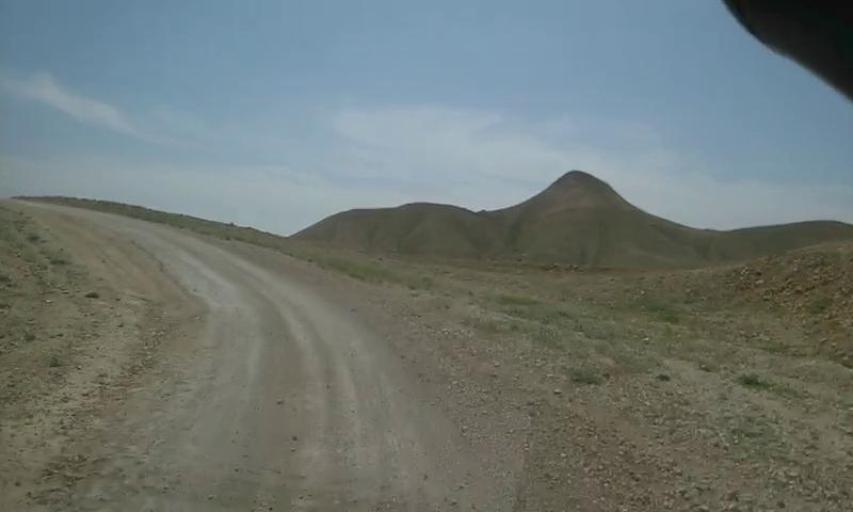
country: PS
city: `Arab ar Rashaydah
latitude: 31.4999
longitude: 35.2940
